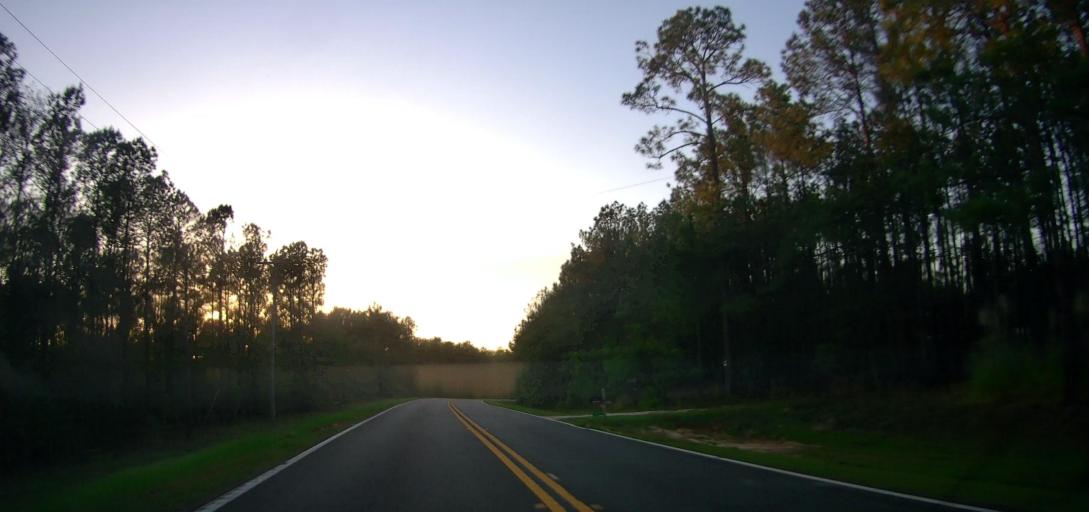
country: US
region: Georgia
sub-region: Marion County
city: Buena Vista
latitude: 32.4270
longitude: -84.5940
